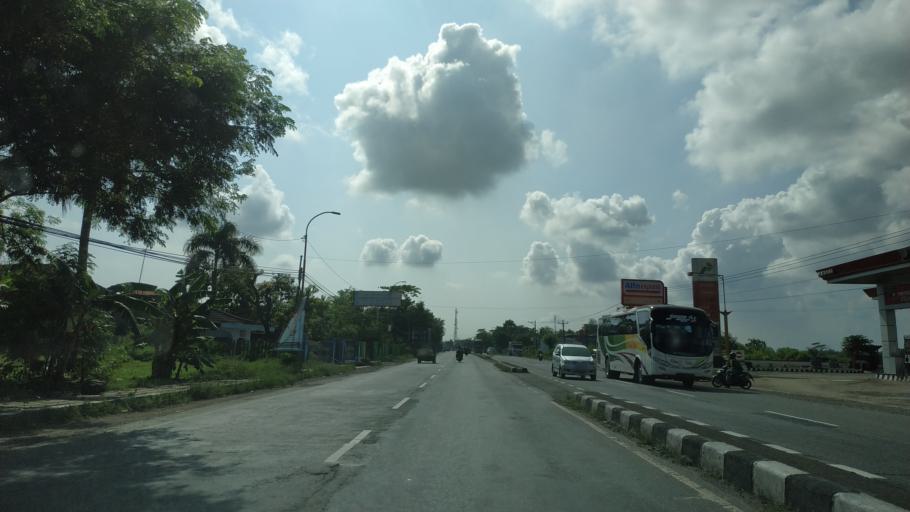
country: ID
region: Central Java
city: Comal
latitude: -6.8854
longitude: 109.5572
